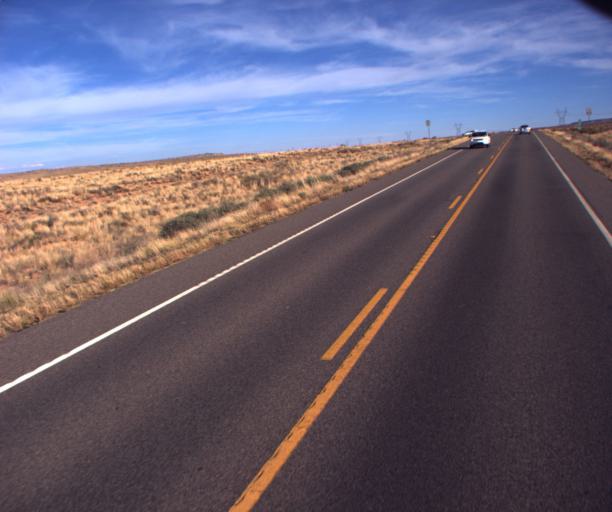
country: US
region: Arizona
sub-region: Apache County
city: Lukachukai
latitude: 36.9395
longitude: -109.2479
